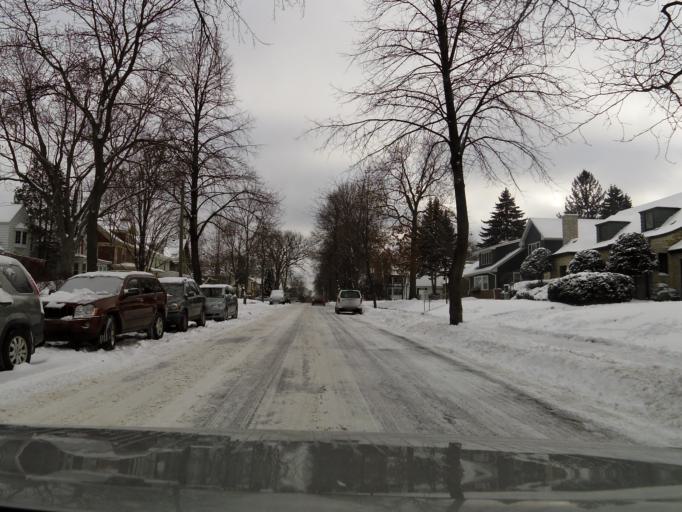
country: US
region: Minnesota
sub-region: Hennepin County
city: Saint Louis Park
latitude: 44.9405
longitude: -93.3009
